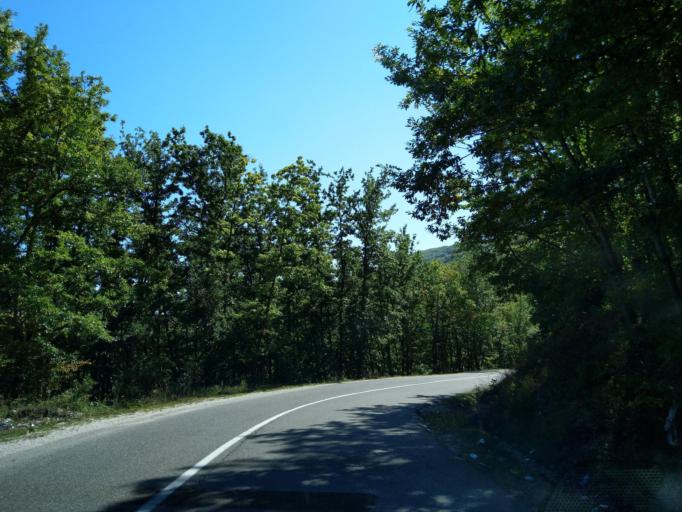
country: RS
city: Sokolovica
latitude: 43.2536
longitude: 20.2561
